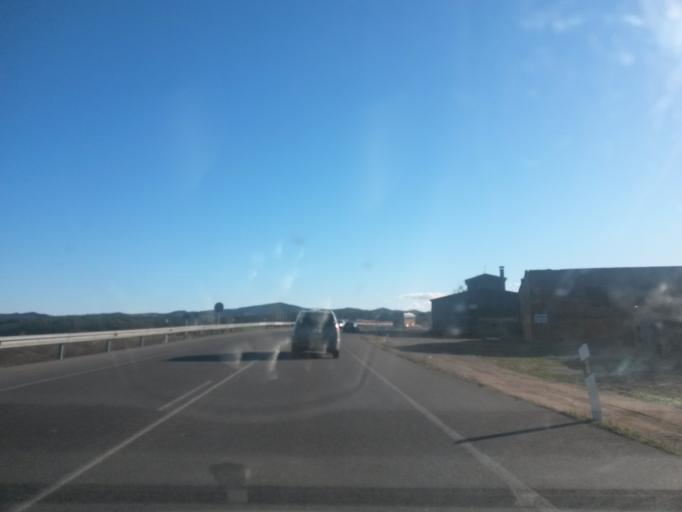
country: ES
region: Catalonia
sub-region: Provincia de Girona
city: Vidreres
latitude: 41.7799
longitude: 2.7593
